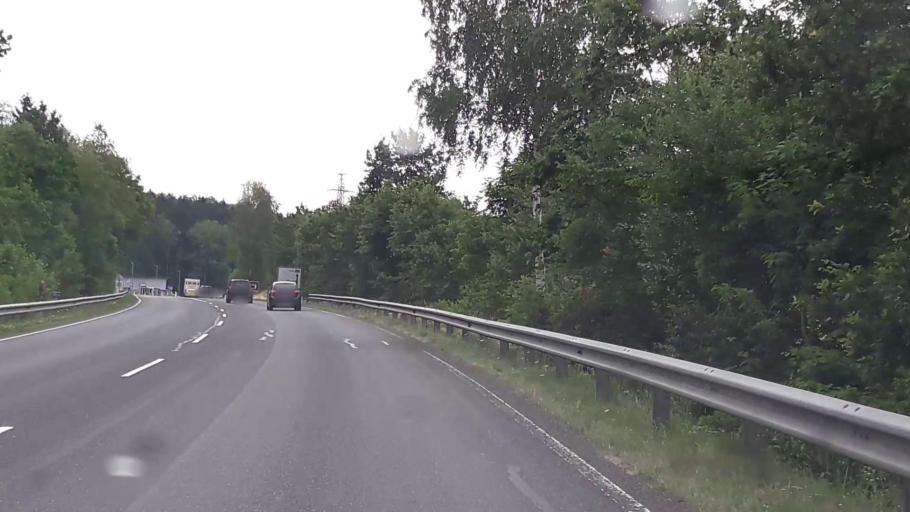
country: AT
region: Upper Austria
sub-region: Politischer Bezirk Rohrbach
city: Kleinzell im Muehlkreis
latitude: 48.4650
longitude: 14.0200
